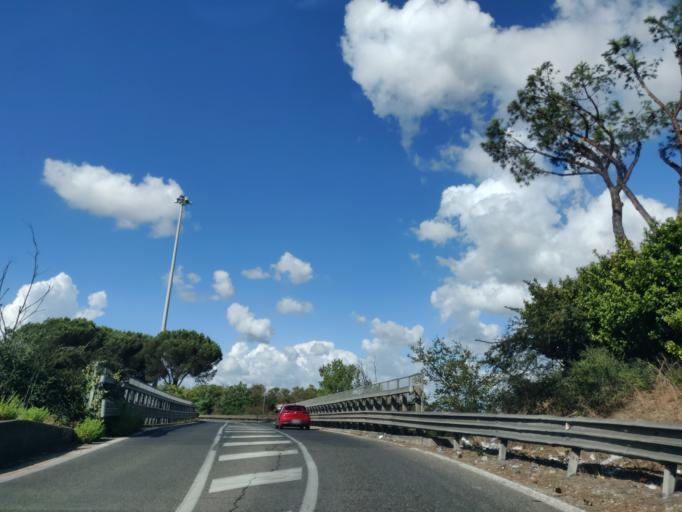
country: IT
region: Latium
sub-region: Citta metropolitana di Roma Capitale
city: La Massimina-Casal Lumbroso
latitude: 41.8857
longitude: 12.3881
